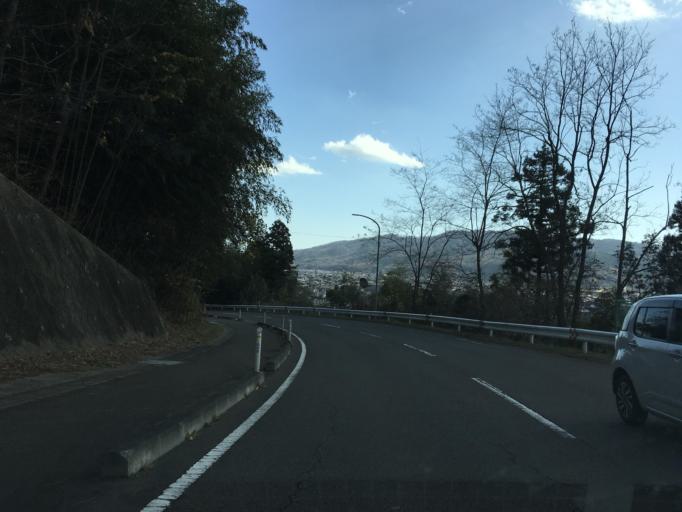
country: JP
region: Miyagi
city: Sendai
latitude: 38.2802
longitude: 140.7593
